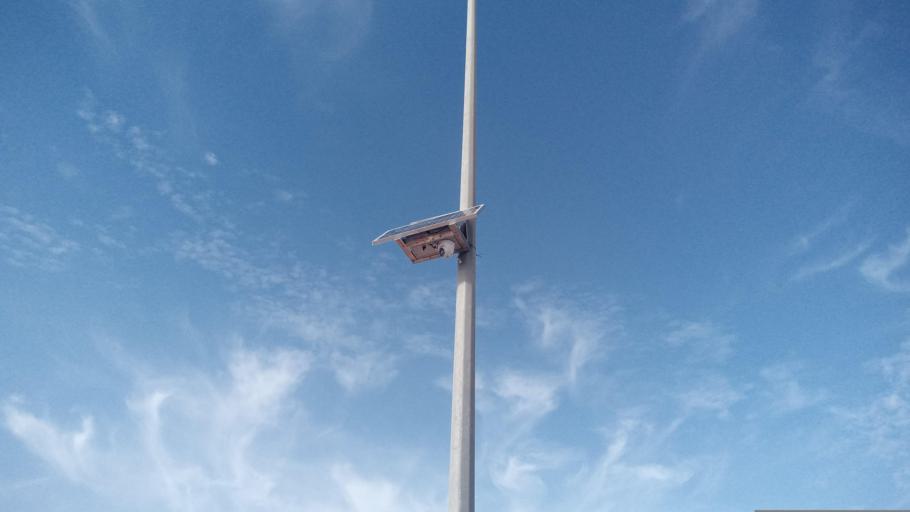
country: TN
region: Madanin
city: Midoun
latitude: 33.7371
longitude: 10.9021
